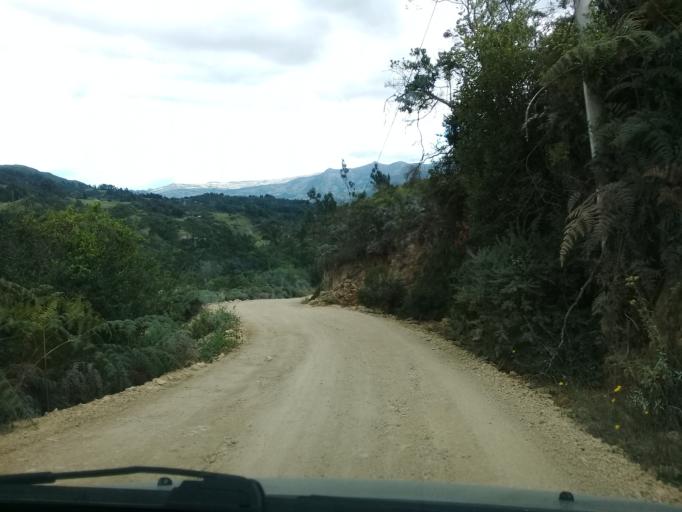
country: CO
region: Cundinamarca
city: Lenguazaque
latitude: 5.2873
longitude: -73.7347
